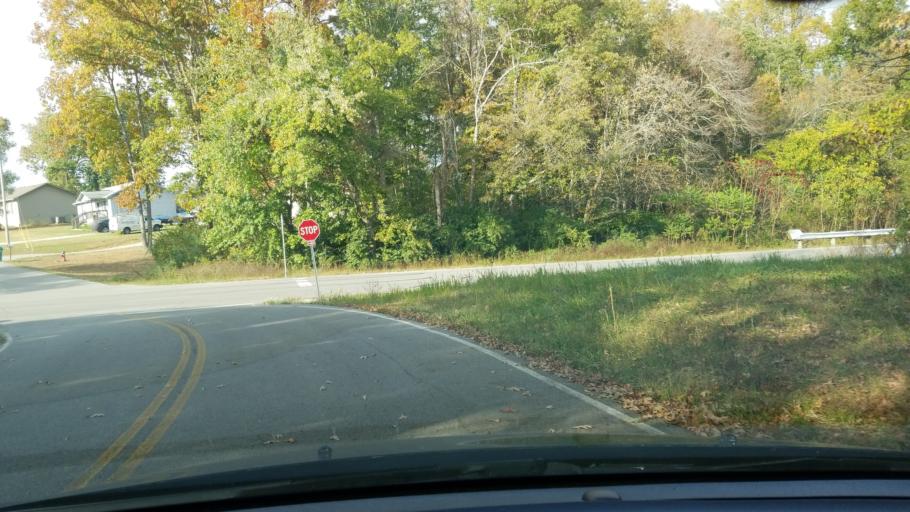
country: US
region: Tennessee
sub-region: Cumberland County
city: Crossville
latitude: 35.9497
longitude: -85.0497
